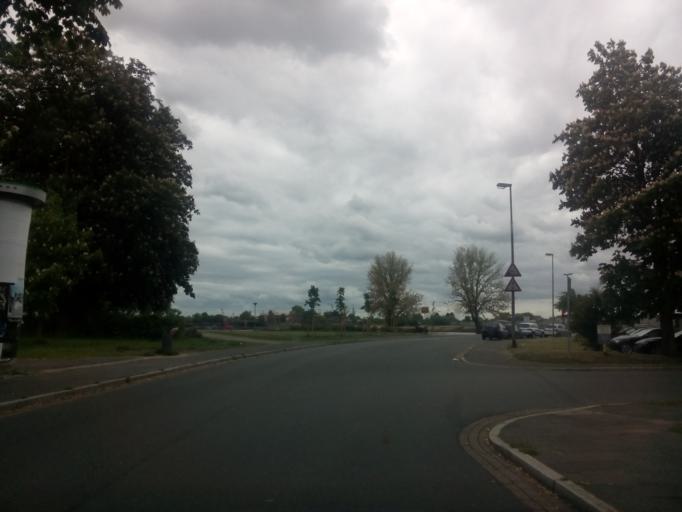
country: DE
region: Lower Saxony
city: Lemwerder
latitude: 53.1826
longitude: 8.5618
